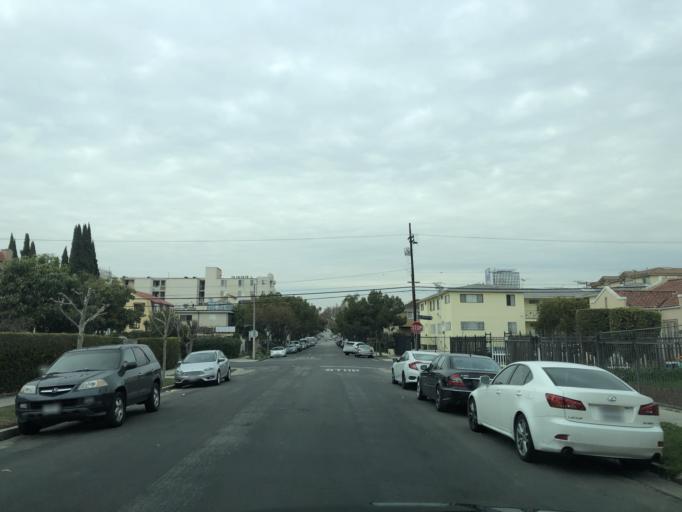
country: US
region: California
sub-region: Los Angeles County
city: Hollywood
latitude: 34.0540
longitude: -118.3122
